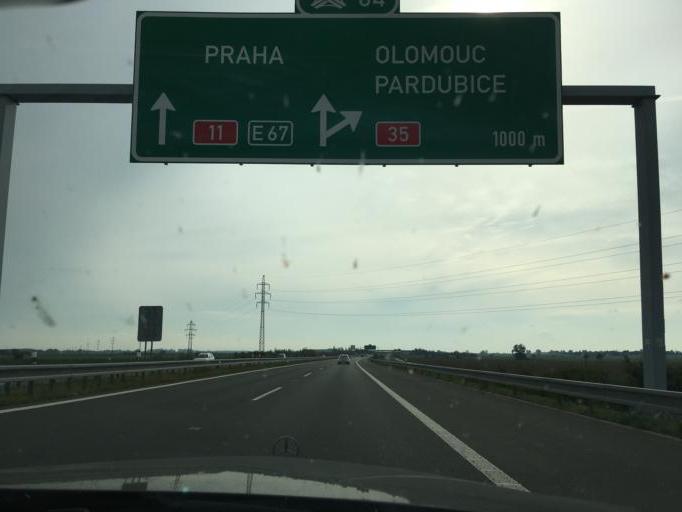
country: CZ
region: Pardubicky
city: Opatovice nad Labem
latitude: 50.1620
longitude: 15.7533
